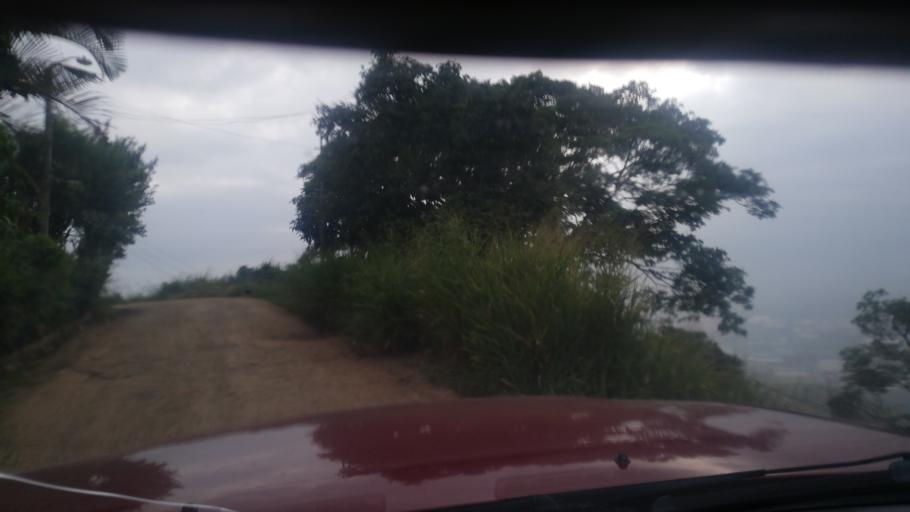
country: CO
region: Valle del Cauca
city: Cali
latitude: 3.5069
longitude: -76.5425
